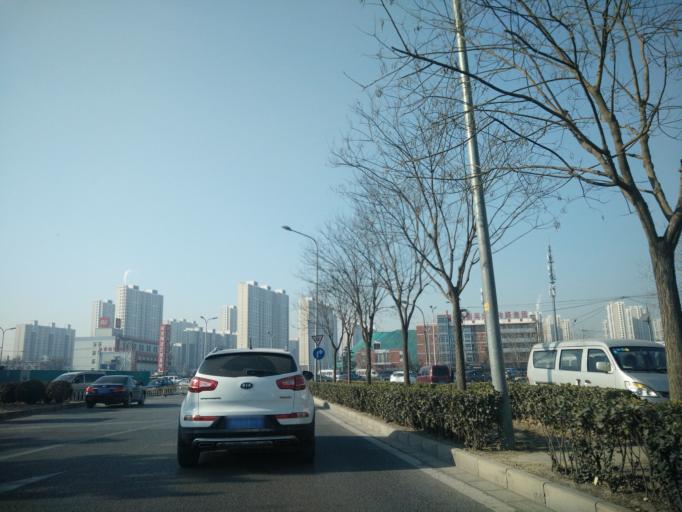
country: CN
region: Beijing
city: Longtan
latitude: 39.8597
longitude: 116.4824
